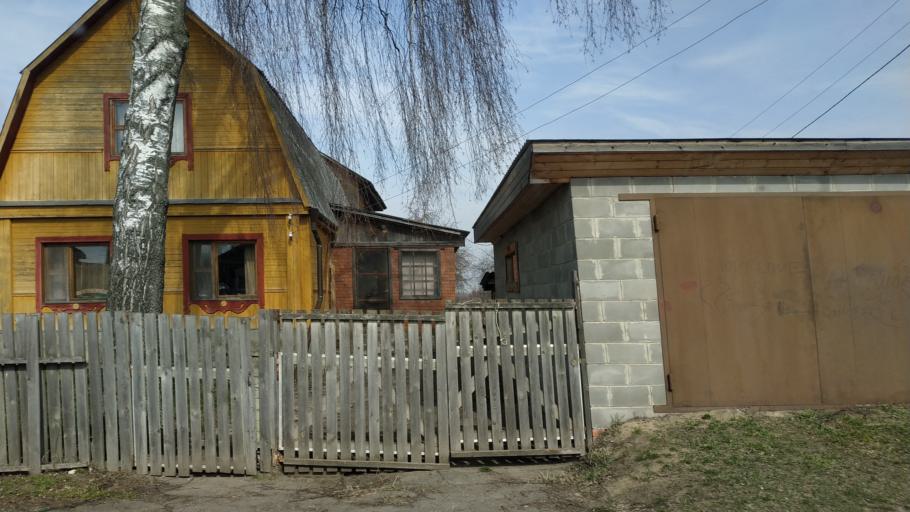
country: RU
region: Moskovskaya
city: Troitskoye
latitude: 55.3619
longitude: 38.5581
